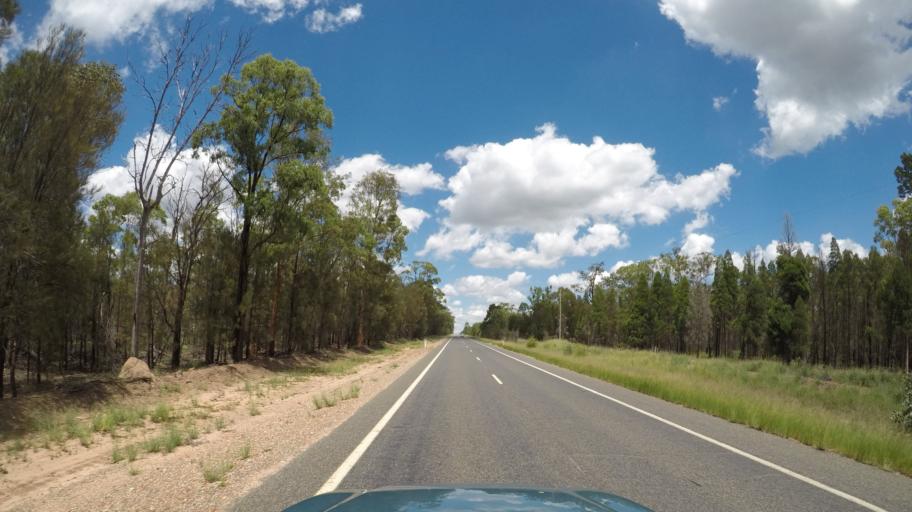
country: AU
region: Queensland
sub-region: Goondiwindi
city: Goondiwindi
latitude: -27.9965
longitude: 150.9473
